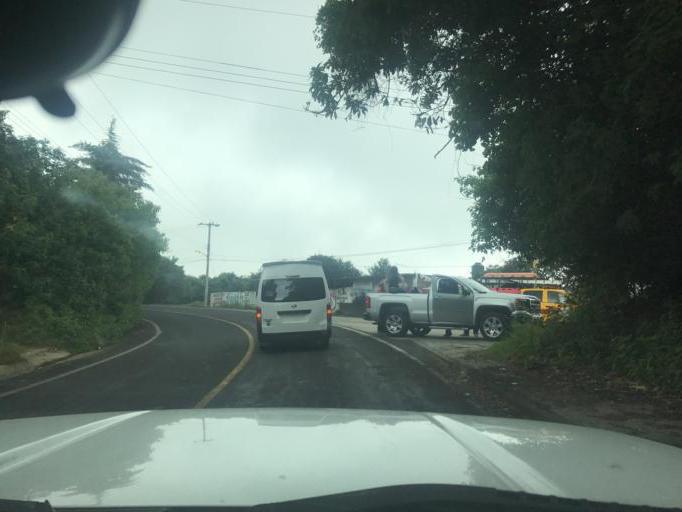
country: MX
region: Morelos
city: Ocuituco
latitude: 18.8823
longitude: -98.7646
